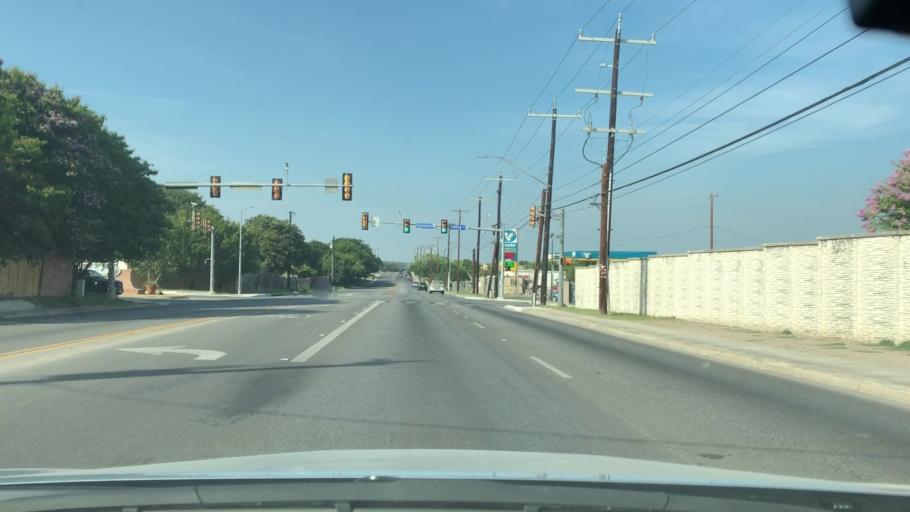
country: US
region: Texas
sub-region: Bexar County
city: Hollywood Park
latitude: 29.5565
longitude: -98.4640
